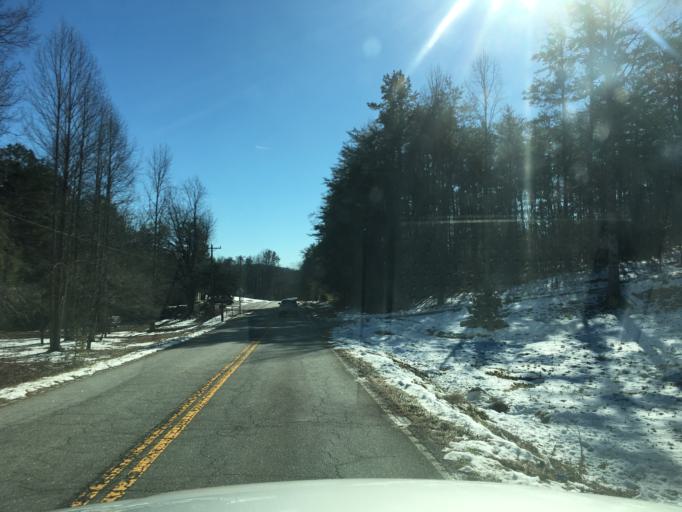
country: US
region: South Carolina
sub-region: Greenville County
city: Slater-Marietta
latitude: 35.0602
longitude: -82.6163
